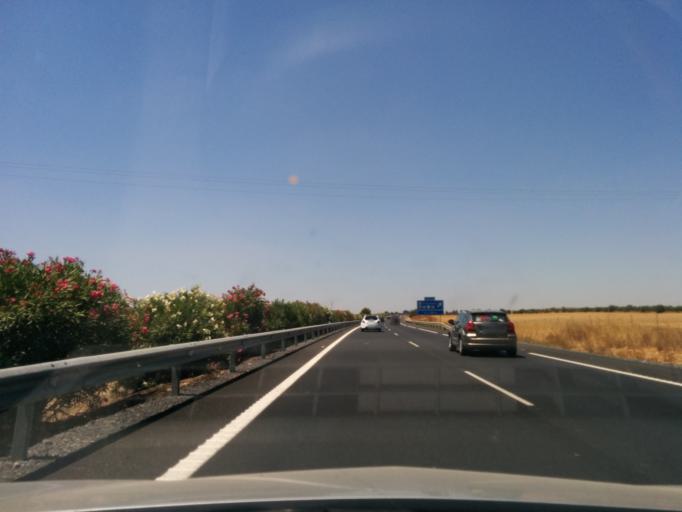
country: ES
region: Andalusia
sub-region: Provincia de Huelva
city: Lucena del Puerto
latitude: 37.3347
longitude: -6.7696
